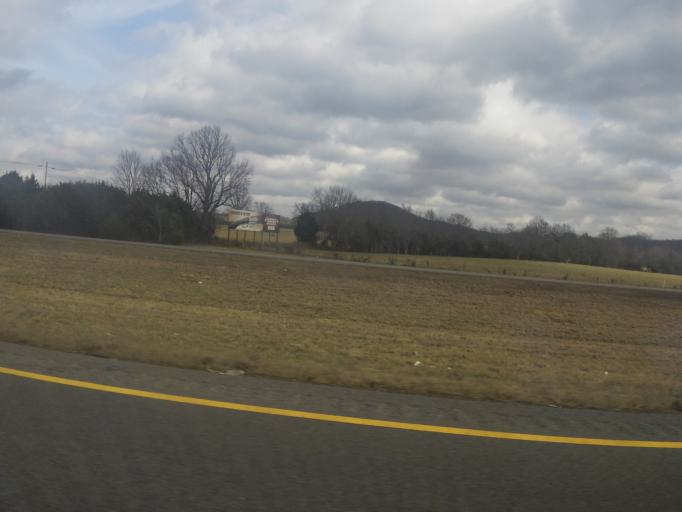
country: US
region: Tennessee
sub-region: Rutherford County
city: Plainview
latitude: 35.6841
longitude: -86.2913
